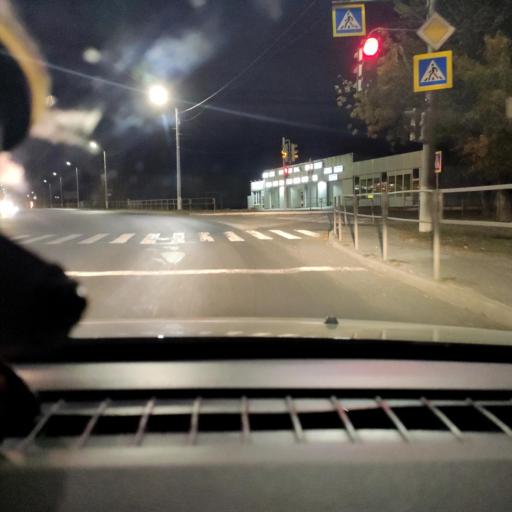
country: RU
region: Samara
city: Novokuybyshevsk
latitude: 53.0906
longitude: 49.9415
